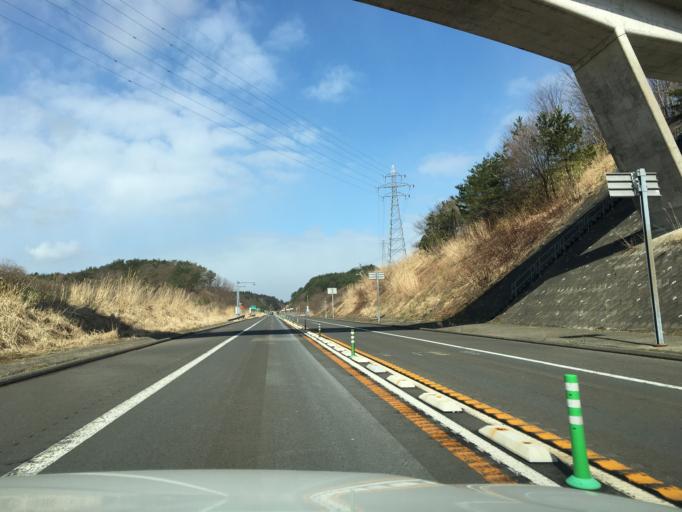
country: JP
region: Akita
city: Akita
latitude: 39.7583
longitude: 140.1338
